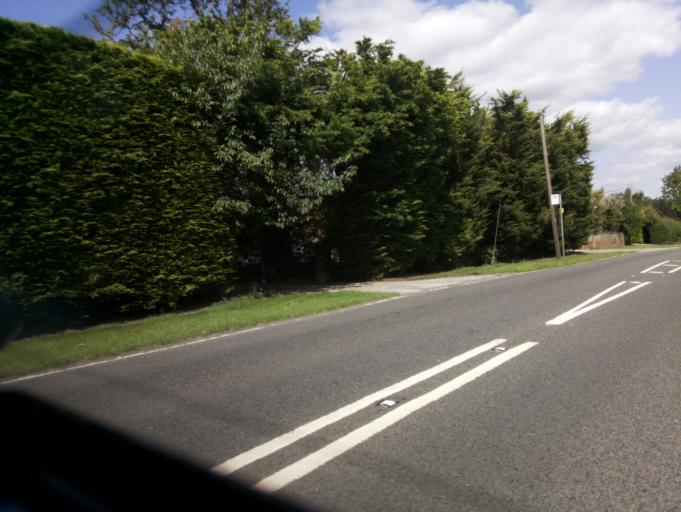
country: GB
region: England
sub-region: Buckinghamshire
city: Aylesbury
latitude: 51.8581
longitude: -0.8302
